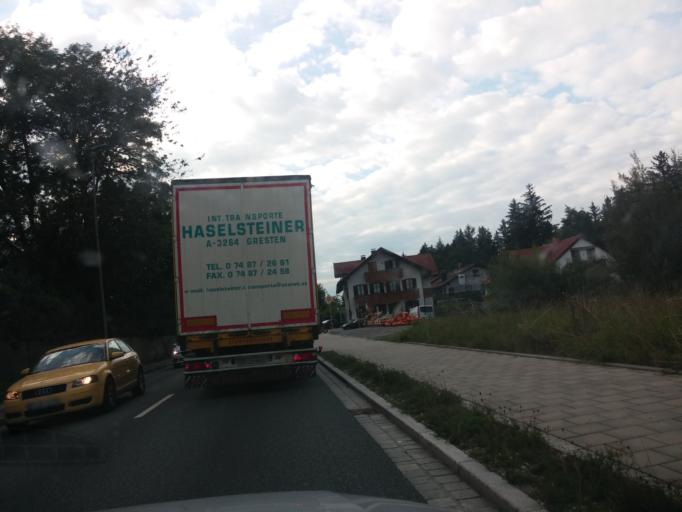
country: DE
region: Bavaria
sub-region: Upper Bavaria
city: Kirchseeon
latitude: 48.0780
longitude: 11.8780
